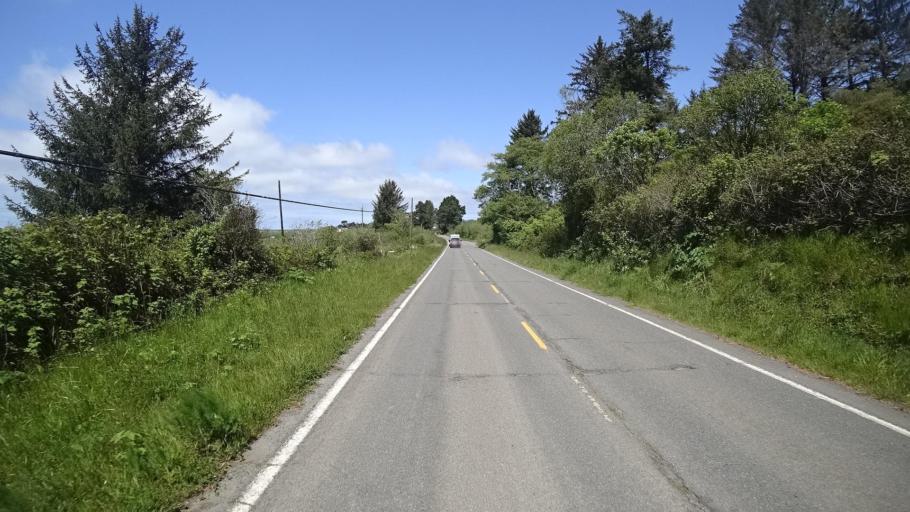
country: US
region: California
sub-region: Humboldt County
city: Ferndale
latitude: 40.6324
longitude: -124.2223
